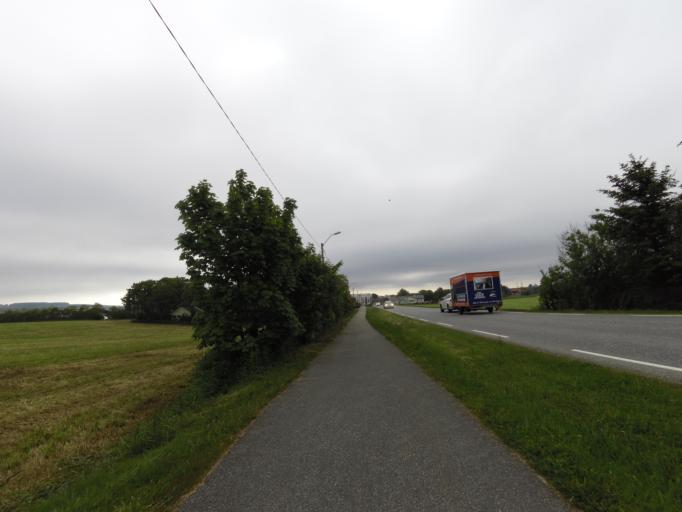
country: NO
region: Rogaland
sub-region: Ha
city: Vigrestad
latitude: 58.5732
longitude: 5.6817
